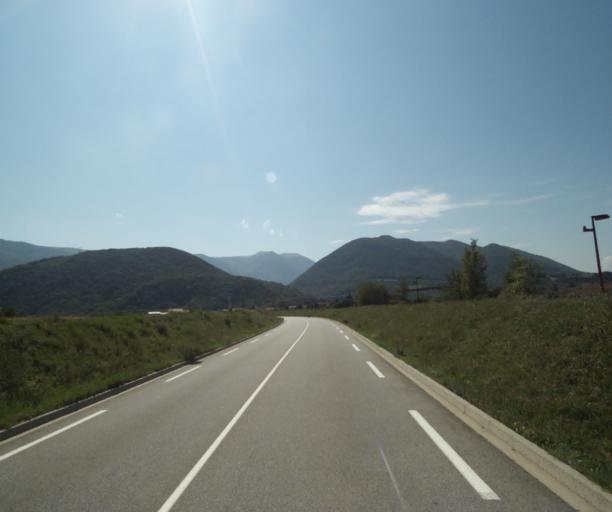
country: FR
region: Rhone-Alpes
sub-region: Departement de l'Isere
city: Vif
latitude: 45.0612
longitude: 5.6778
